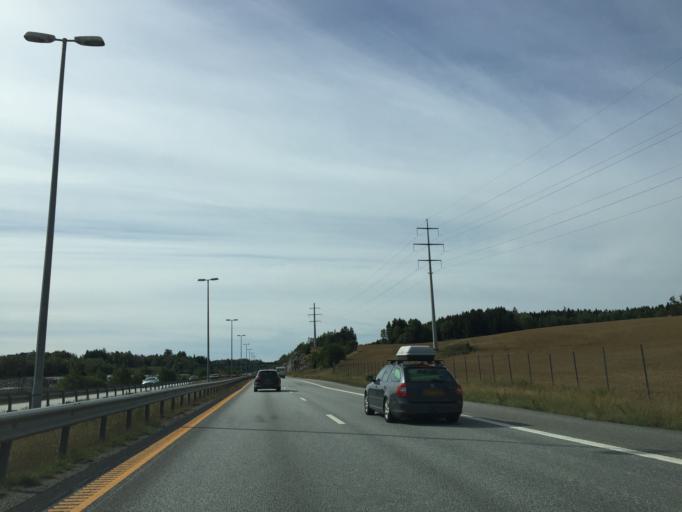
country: NO
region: Akershus
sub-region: Vestby
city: Vestby
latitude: 59.5899
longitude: 10.7370
